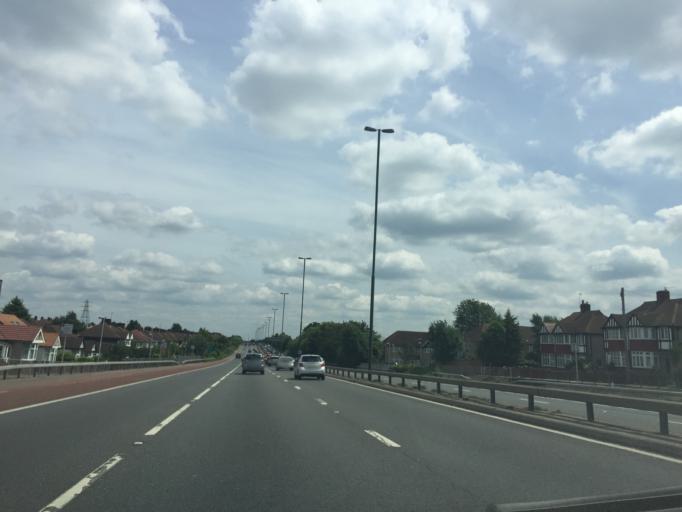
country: GB
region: England
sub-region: Greater London
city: Welling
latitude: 51.4543
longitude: 0.0948
